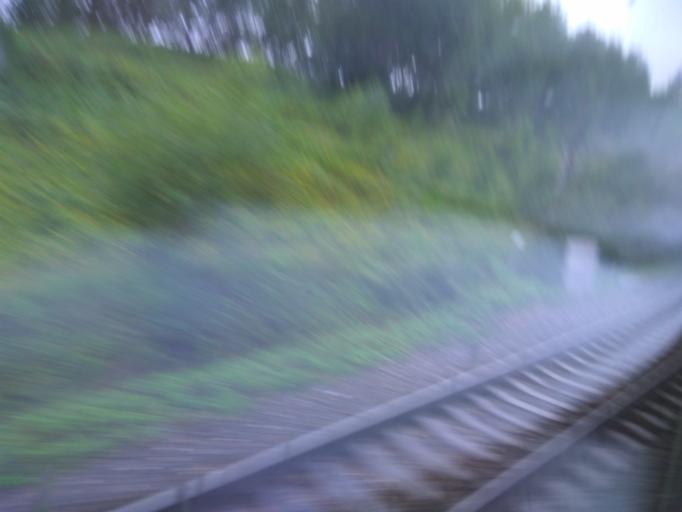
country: RU
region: Moskovskaya
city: Ozherel'ye
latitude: 54.7195
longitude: 38.4313
